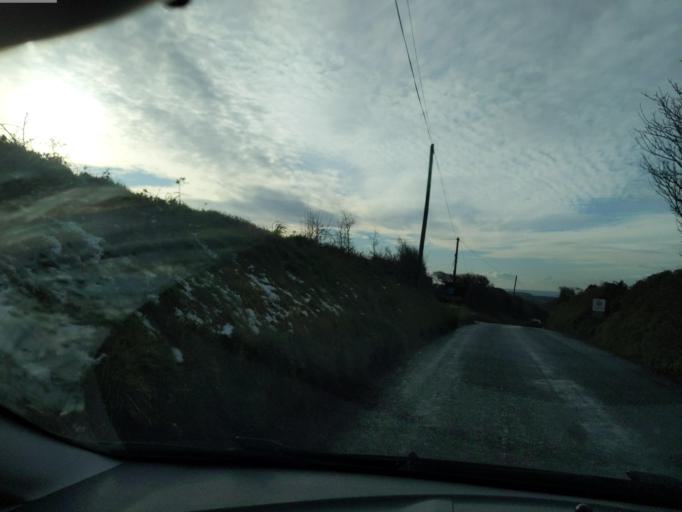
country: GB
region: England
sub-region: Cornwall
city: Camelford
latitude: 50.6981
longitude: -4.6592
